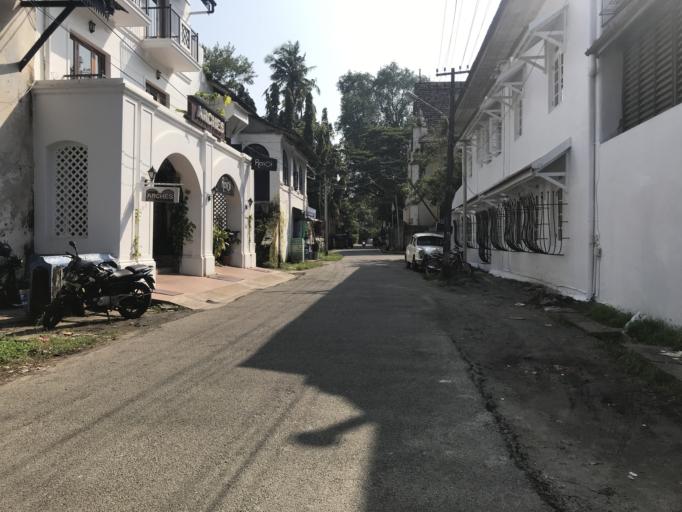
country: IN
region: Kerala
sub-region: Ernakulam
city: Cochin
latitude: 9.9664
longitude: 76.2415
